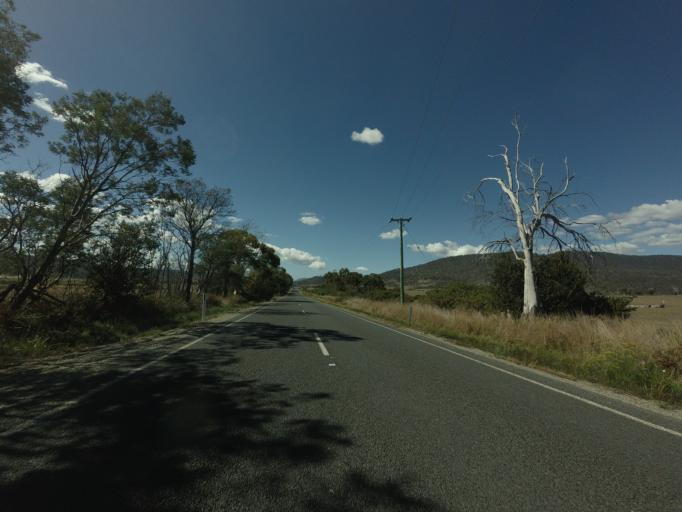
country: AU
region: Tasmania
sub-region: Break O'Day
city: St Helens
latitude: -41.6789
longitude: 147.8916
